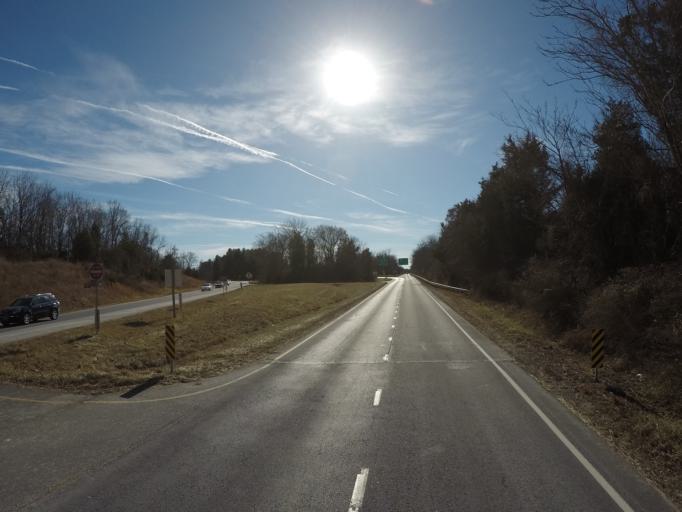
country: US
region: Virginia
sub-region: Loudoun County
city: Leesburg
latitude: 39.1394
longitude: -77.5473
